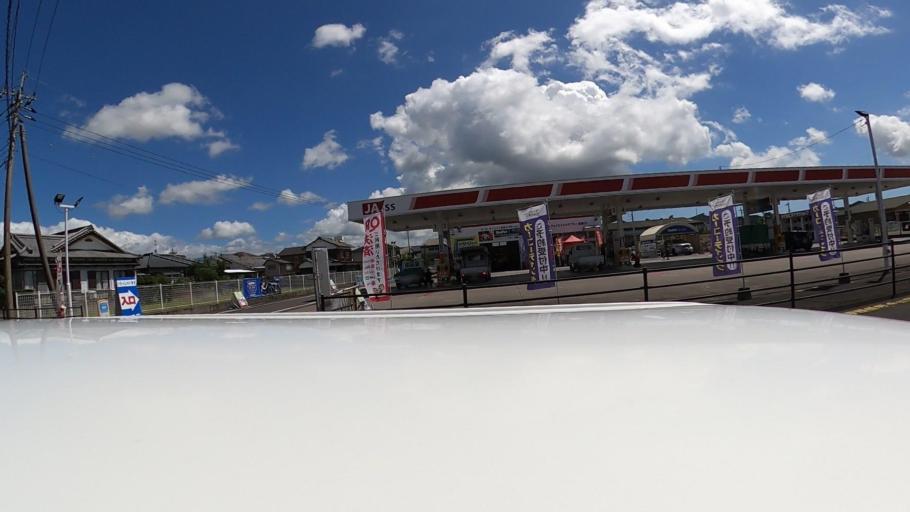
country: JP
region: Miyazaki
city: Tsuma
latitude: 32.1027
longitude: 131.4020
